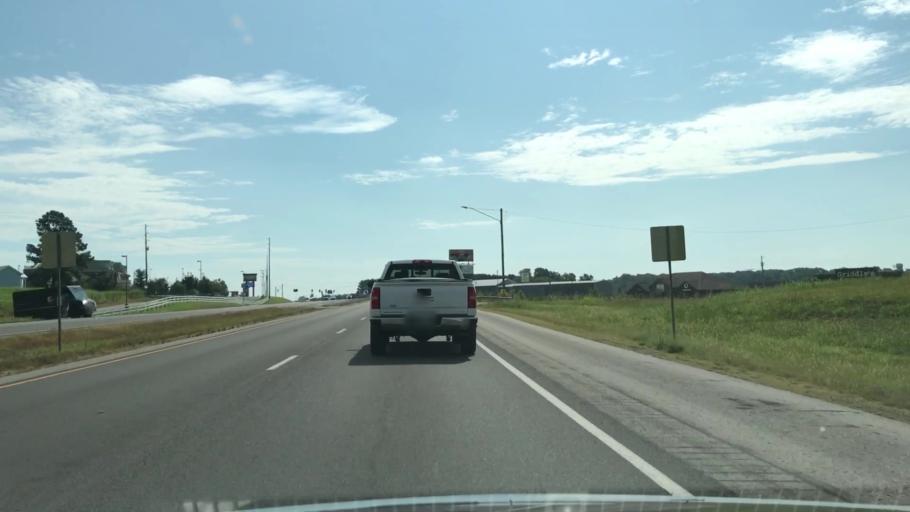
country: US
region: Kentucky
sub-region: Allen County
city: Scottsville
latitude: 36.7570
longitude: -86.2223
